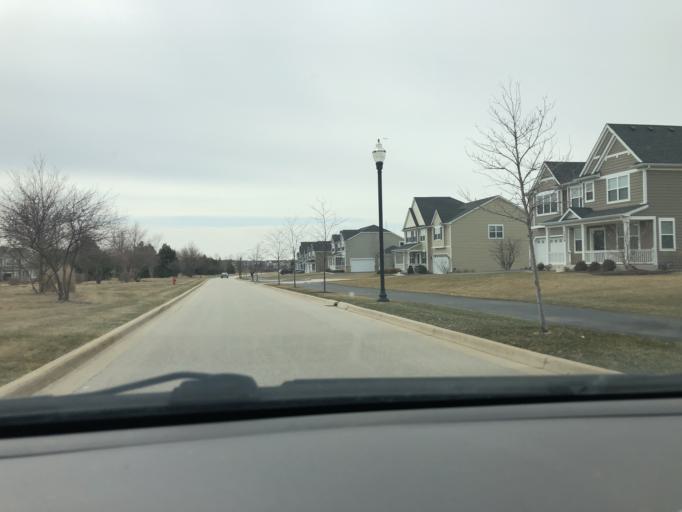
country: US
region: Illinois
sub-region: Kane County
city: Pingree Grove
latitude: 42.0300
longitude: -88.3589
